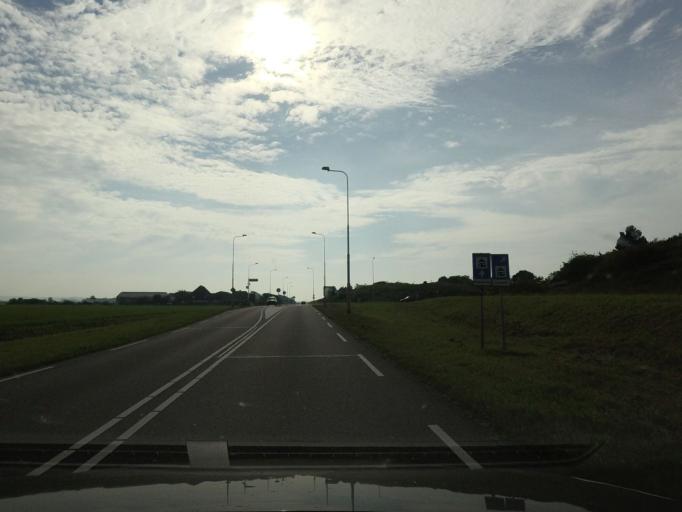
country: NL
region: North Holland
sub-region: Gemeente Schagen
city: Harenkarspel
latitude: 52.7720
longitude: 4.6709
